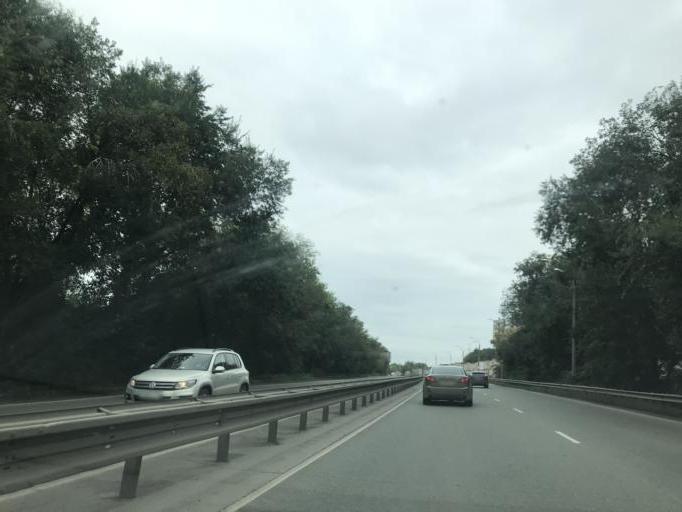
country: RU
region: Chelyabinsk
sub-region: Gorod Chelyabinsk
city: Chelyabinsk
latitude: 55.1715
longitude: 61.4270
